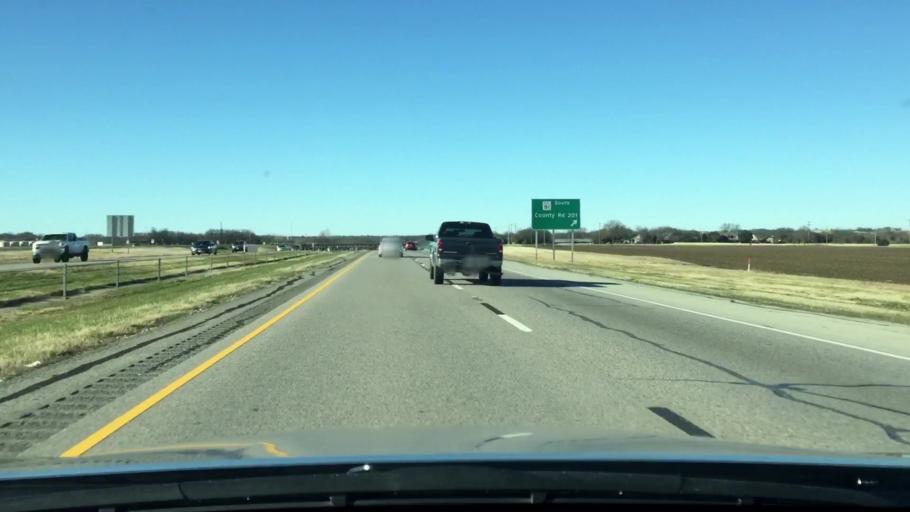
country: US
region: Texas
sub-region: Johnson County
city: Grandview
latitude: 32.2826
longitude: -97.1754
